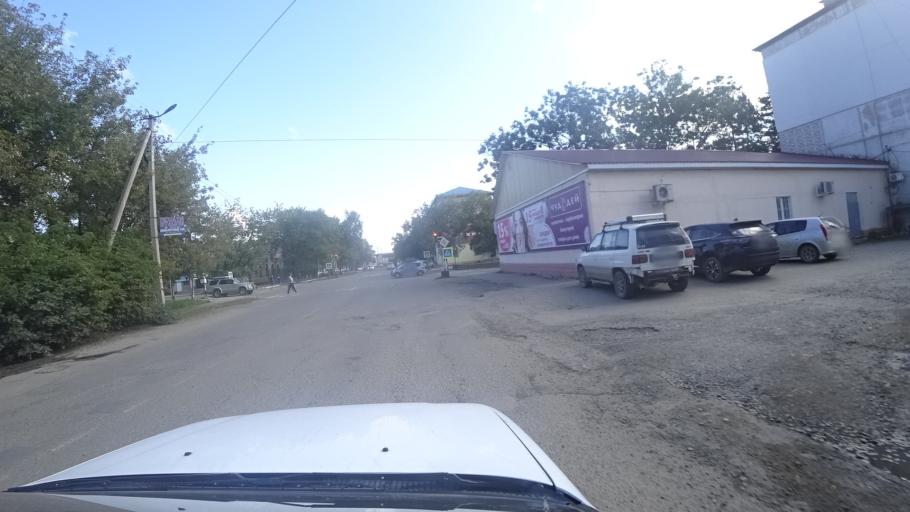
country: RU
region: Primorskiy
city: Dal'nerechensk
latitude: 45.9340
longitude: 133.7347
